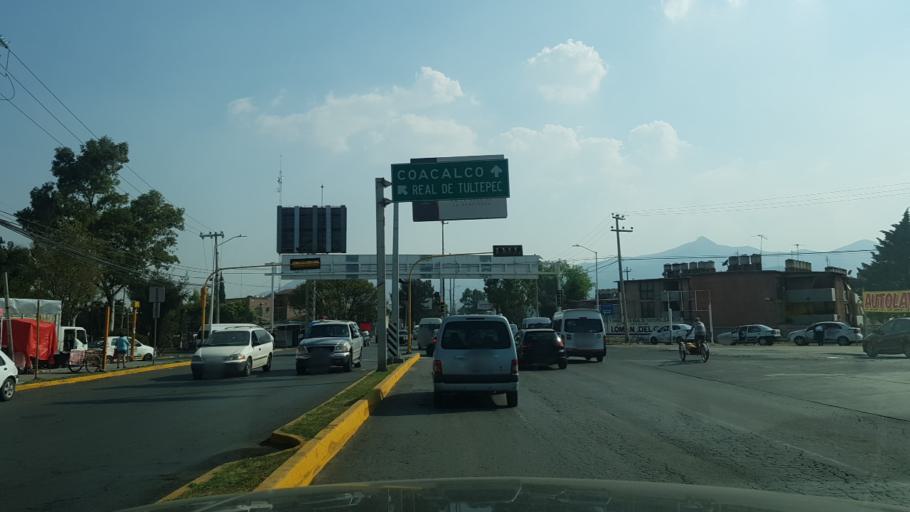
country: MX
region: Mexico
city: Santiago Teyahualco
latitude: 19.6535
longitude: -99.1197
